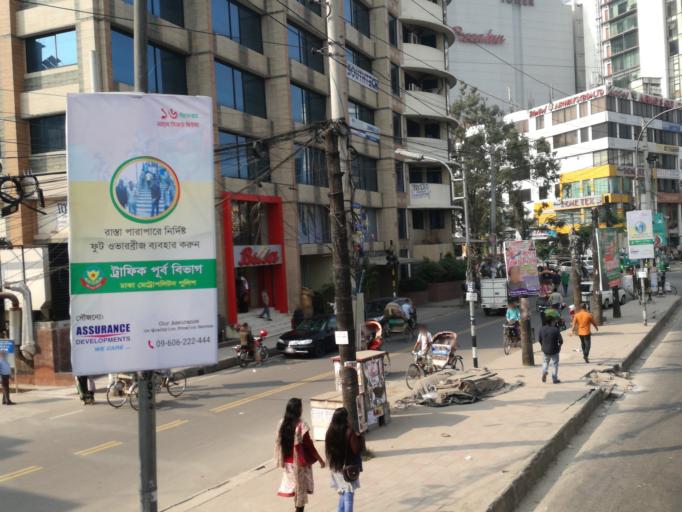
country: BD
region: Dhaka
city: Tungi
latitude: 23.8602
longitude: 90.4005
